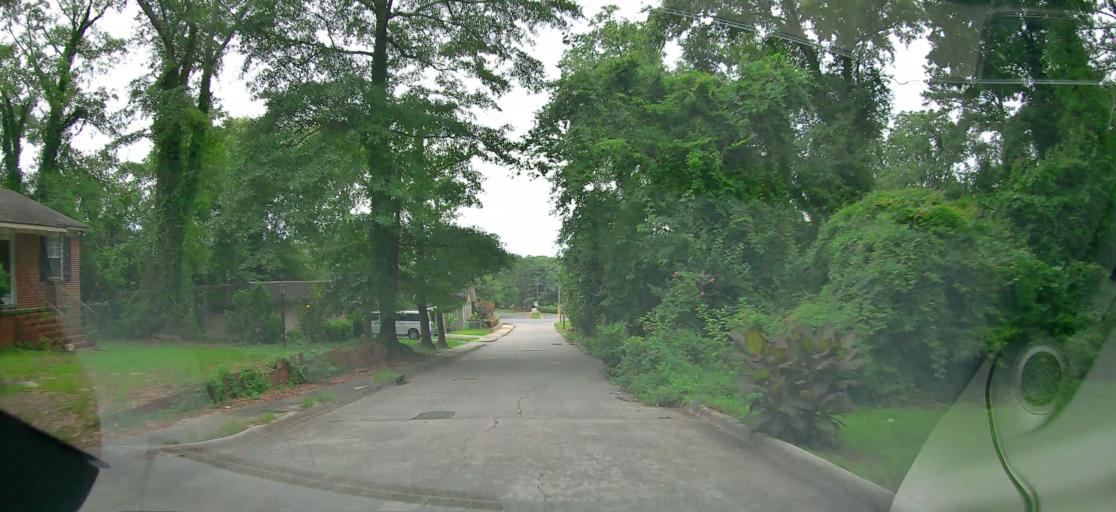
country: US
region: Georgia
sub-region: Bibb County
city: Macon
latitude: 32.8528
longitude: -83.6256
